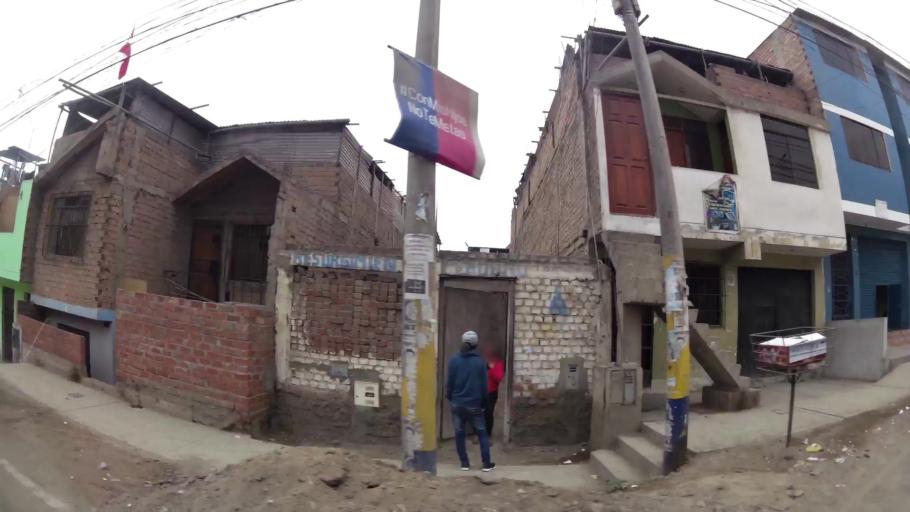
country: PE
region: Lima
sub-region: Lima
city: Surco
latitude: -12.1387
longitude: -76.9585
